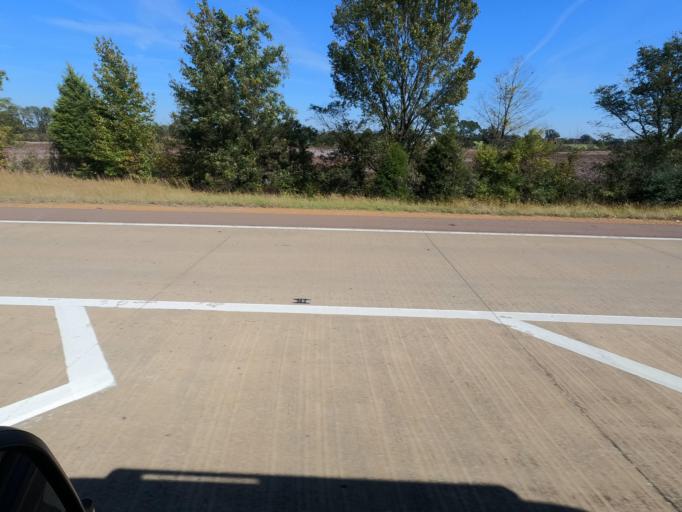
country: US
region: Tennessee
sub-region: Dyer County
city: Dyersburg
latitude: 35.9687
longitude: -89.3335
